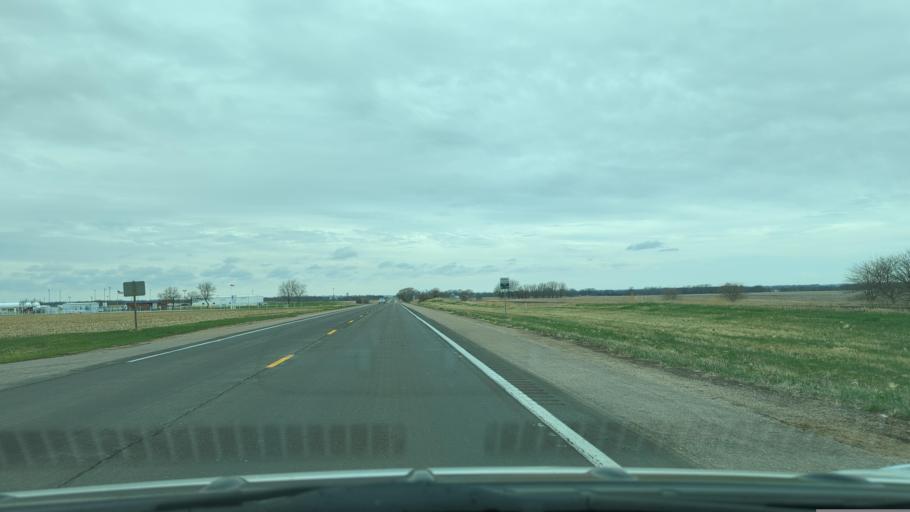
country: US
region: Nebraska
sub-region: Lancaster County
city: Waverly
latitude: 40.9466
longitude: -96.4637
